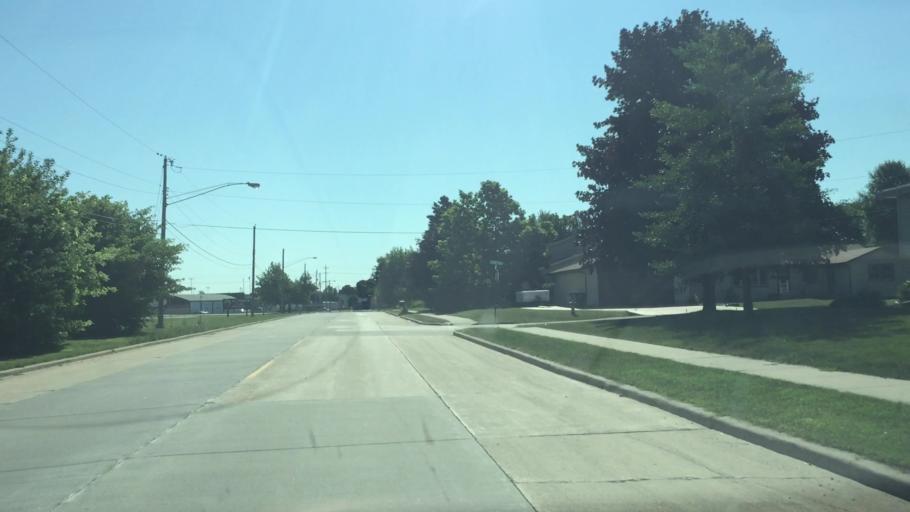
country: US
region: Wisconsin
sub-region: Winnebago County
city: Menasha
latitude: 44.2226
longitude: -88.4318
